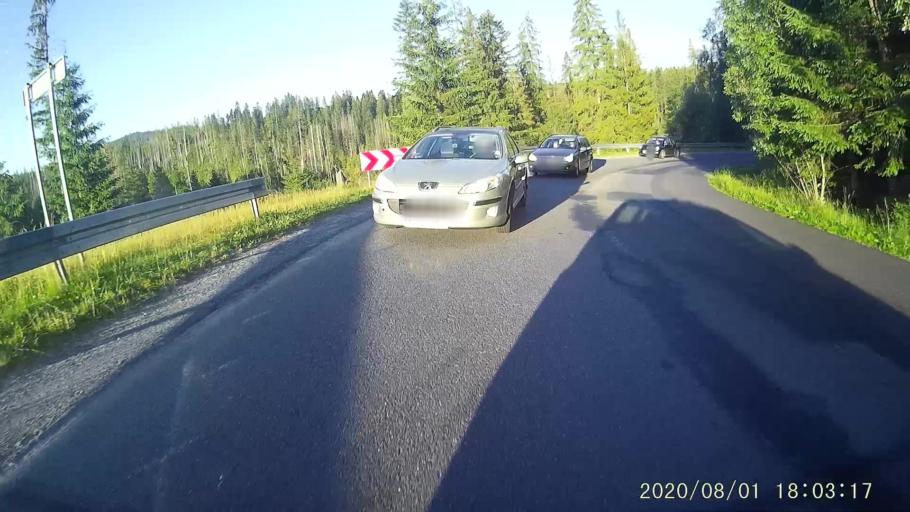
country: PL
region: Lesser Poland Voivodeship
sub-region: Powiat tatrzanski
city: Bukowina Tatrzanska
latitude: 49.2930
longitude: 20.0614
